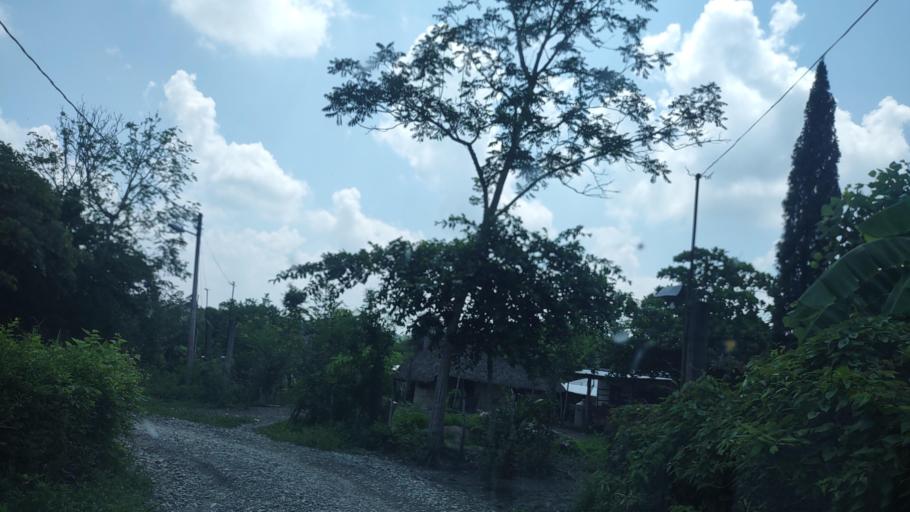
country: MX
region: Veracruz
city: Tempoal de Sanchez
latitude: 21.5468
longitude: -98.2739
